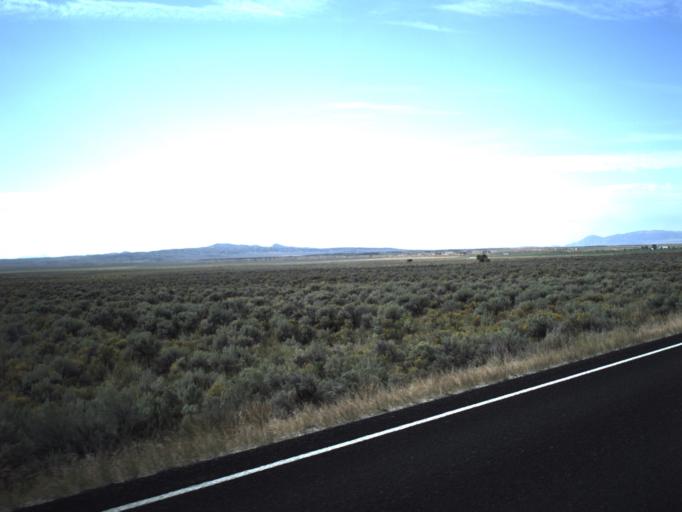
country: US
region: Idaho
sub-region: Cassia County
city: Burley
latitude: 41.7892
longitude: -113.4743
